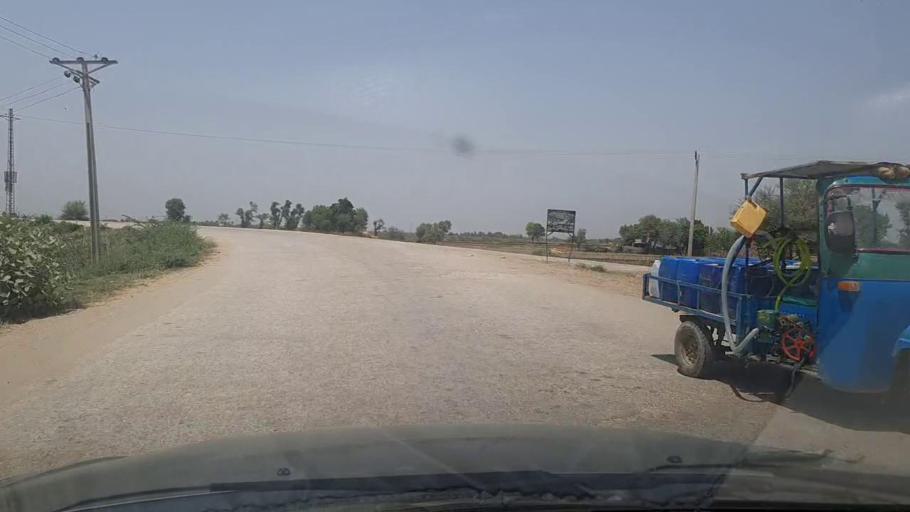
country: PK
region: Sindh
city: Bhiria
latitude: 26.8886
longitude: 68.2673
